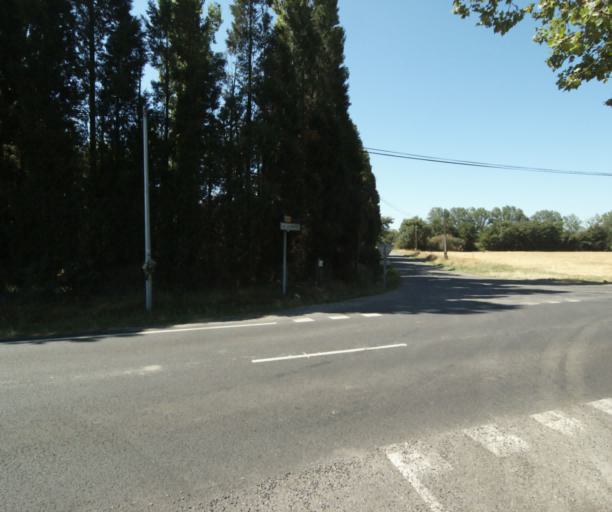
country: FR
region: Midi-Pyrenees
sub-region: Departement de la Haute-Garonne
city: Revel
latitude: 43.4672
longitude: 1.9762
